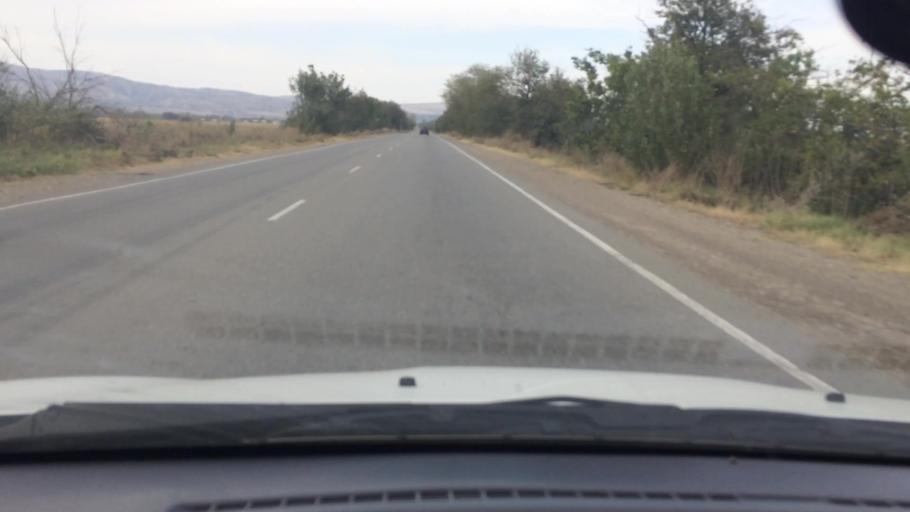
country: GE
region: Kvemo Kartli
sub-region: Marneuli
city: Marneuli
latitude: 41.5583
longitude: 44.7760
